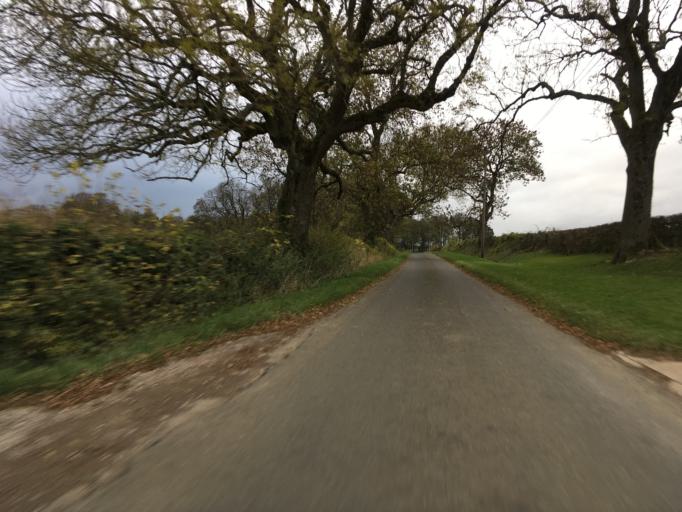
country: GB
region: England
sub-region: South Gloucestershire
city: Hinton
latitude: 51.4856
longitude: -2.3589
